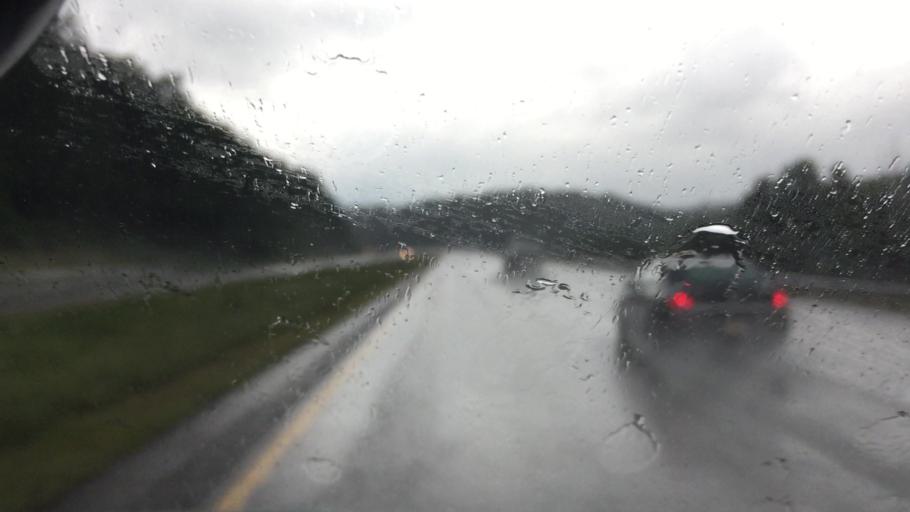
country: US
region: West Virginia
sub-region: Preston County
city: Terra Alta
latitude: 39.6620
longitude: -79.4679
